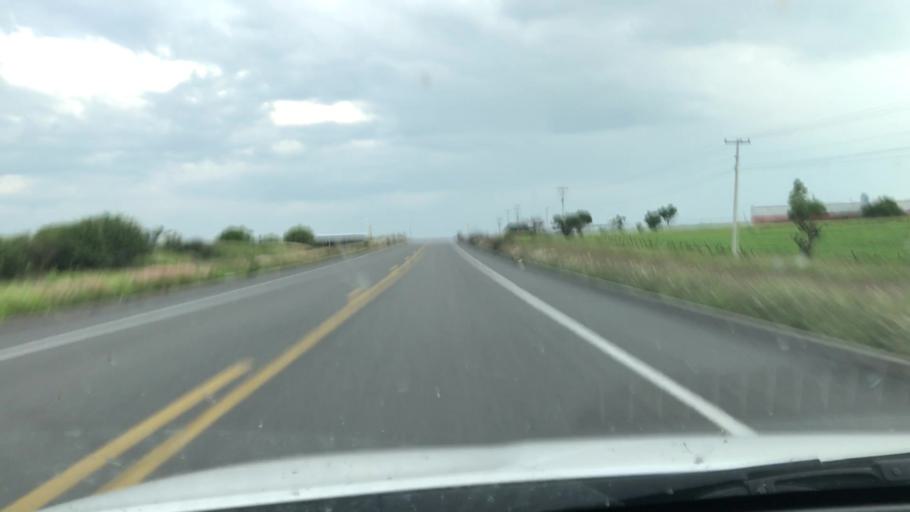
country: MX
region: Jalisco
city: Degollado
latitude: 20.3523
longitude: -102.1549
